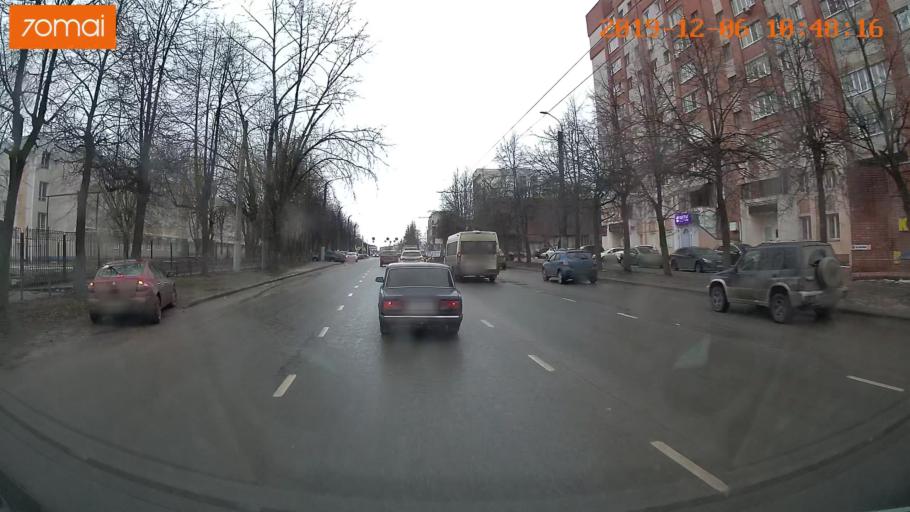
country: RU
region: Ivanovo
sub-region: Gorod Ivanovo
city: Ivanovo
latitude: 56.9959
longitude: 40.9692
